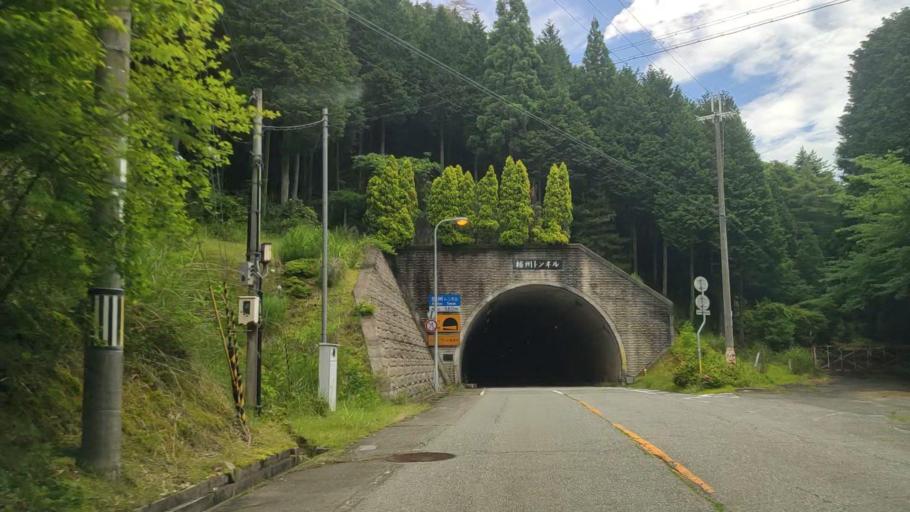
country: JP
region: Kyoto
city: Fukuchiyama
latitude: 35.2110
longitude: 134.9425
